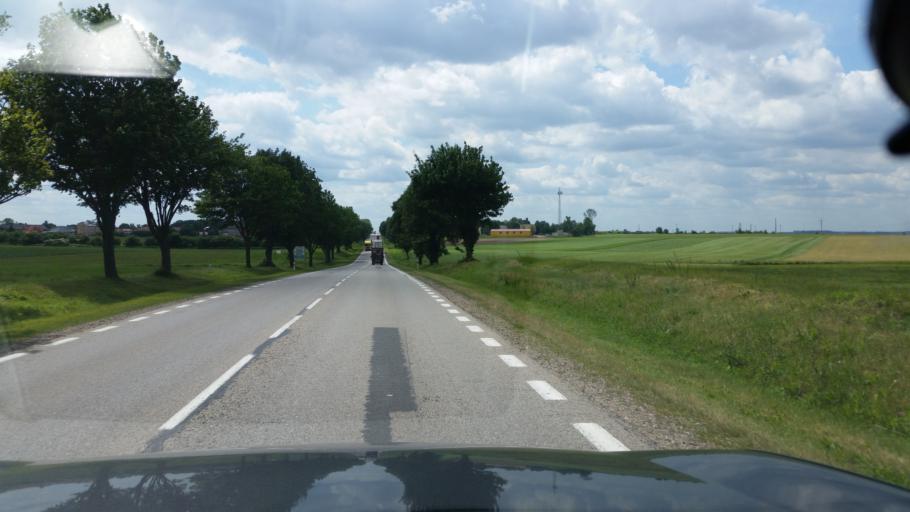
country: PL
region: Podlasie
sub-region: Powiat lomzynski
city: Piatnica
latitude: 53.2177
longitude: 22.1069
